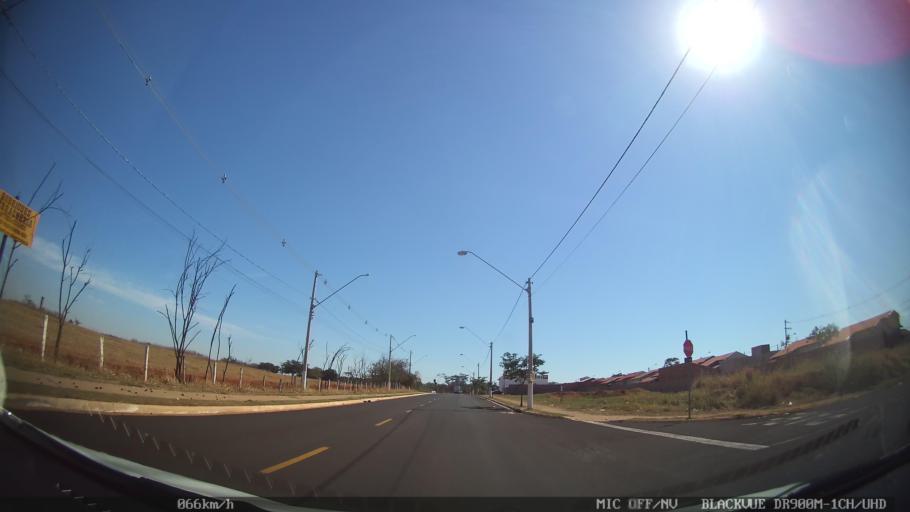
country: BR
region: Sao Paulo
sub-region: Sao Jose Do Rio Preto
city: Sao Jose do Rio Preto
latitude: -20.7521
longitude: -49.4402
